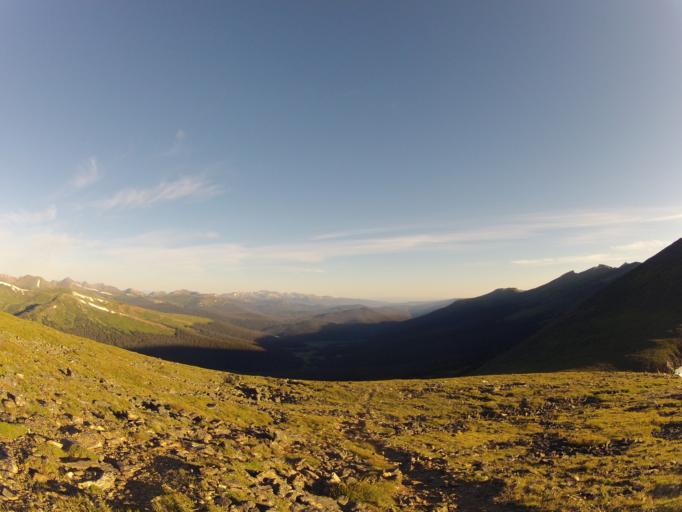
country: US
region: Colorado
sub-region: Larimer County
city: Estes Park
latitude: 40.4365
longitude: -105.7024
